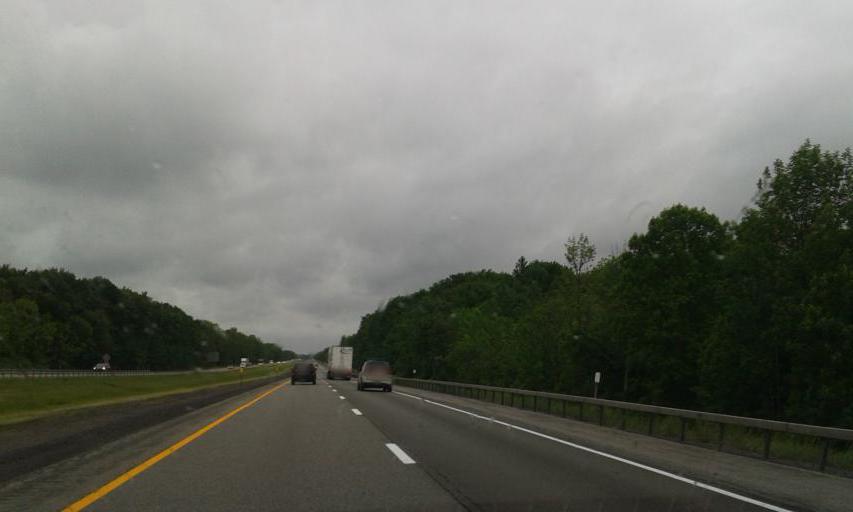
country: US
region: New York
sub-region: Erie County
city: Akron
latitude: 42.9921
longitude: -78.4356
